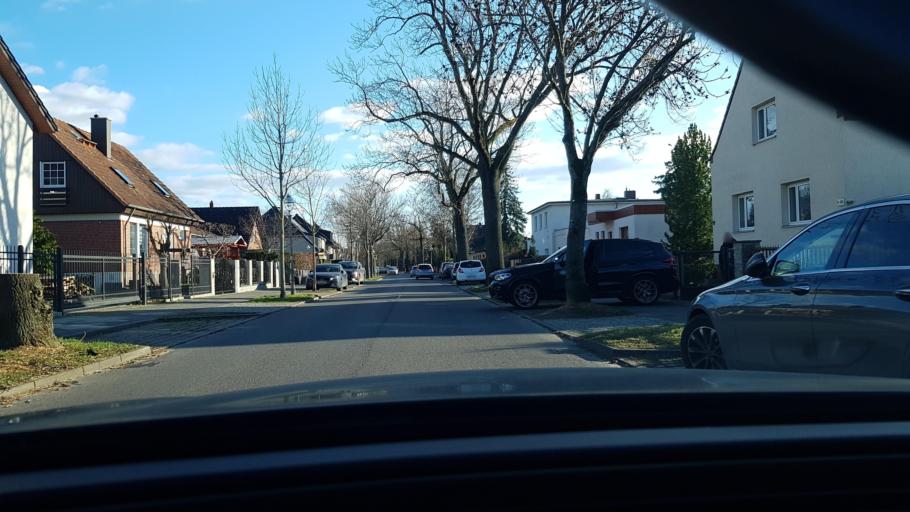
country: DE
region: Berlin
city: Rudow
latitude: 52.4114
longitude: 13.4984
